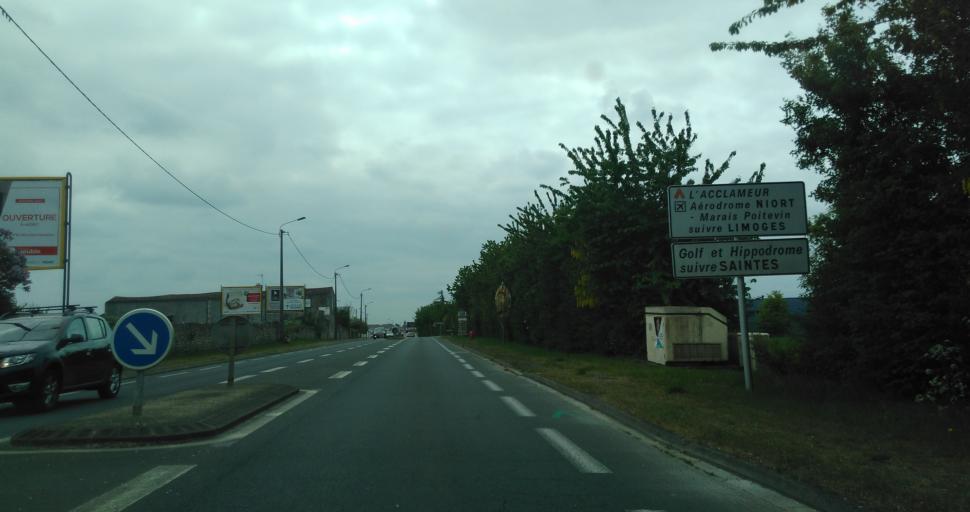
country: FR
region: Poitou-Charentes
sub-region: Departement des Deux-Sevres
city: Niort
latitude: 46.3452
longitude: -0.4438
